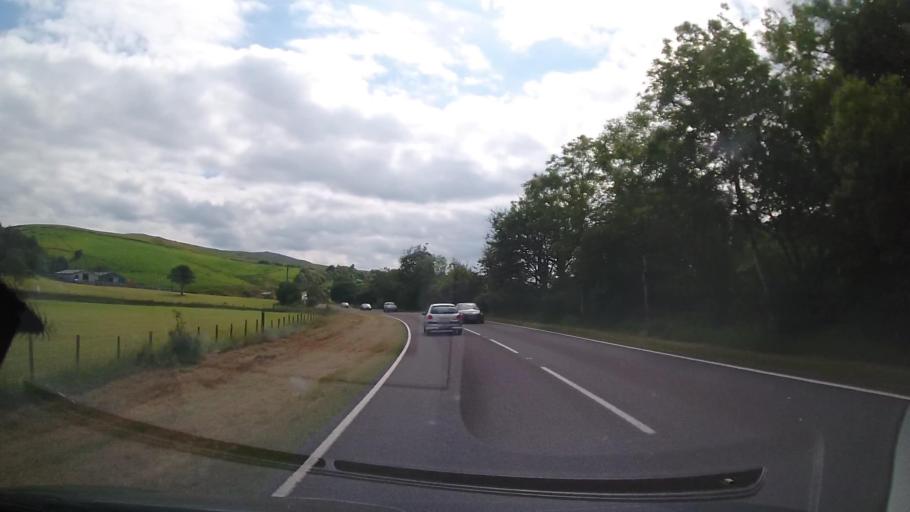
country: GB
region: Wales
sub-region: Gwynedd
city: Trawsfynydd
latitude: 52.9130
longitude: -3.8497
